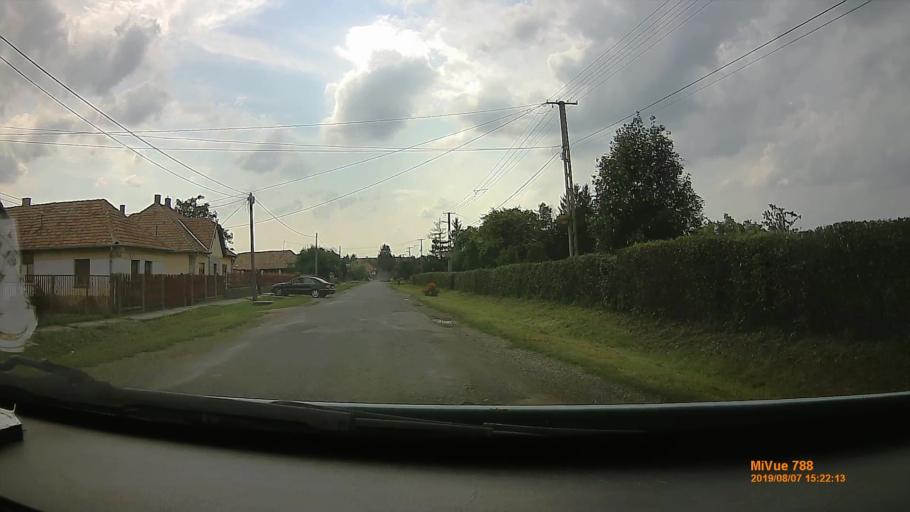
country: HU
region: Borsod-Abauj-Zemplen
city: Encs
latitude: 48.3612
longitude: 21.1455
